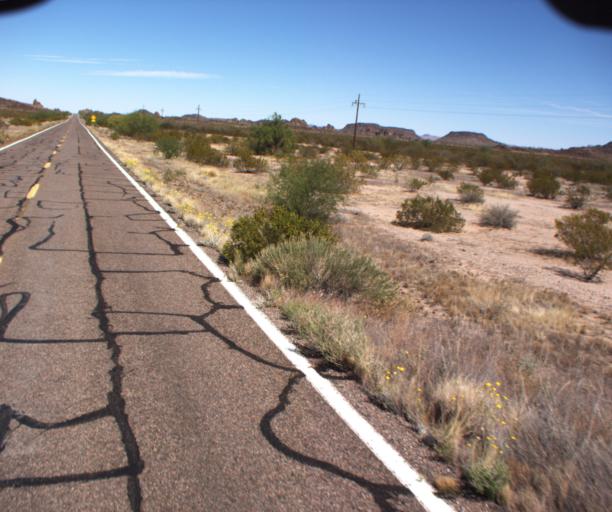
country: US
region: Arizona
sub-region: Pima County
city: Ajo
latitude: 32.5284
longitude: -112.8803
